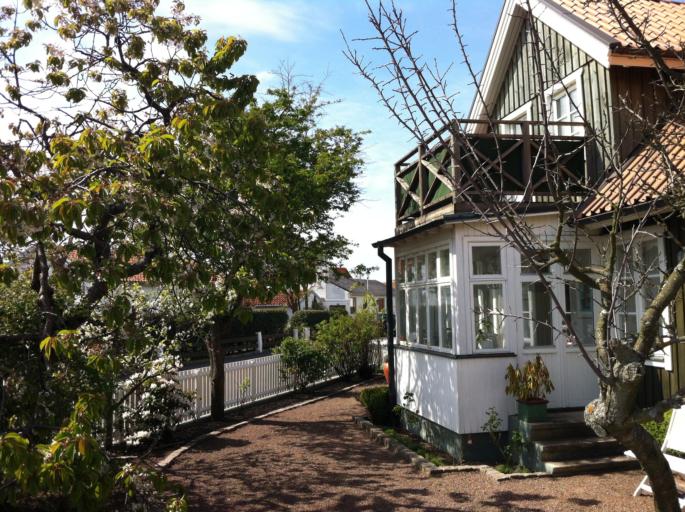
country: SE
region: Skane
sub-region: Hoganas Kommun
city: Hoganas
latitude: 56.1454
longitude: 12.5703
